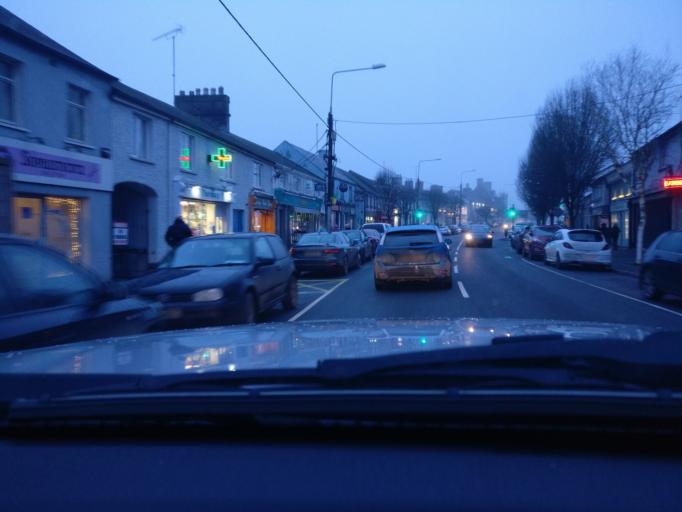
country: IE
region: Leinster
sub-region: An Mhi
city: Athboy
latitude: 53.6219
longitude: -6.9208
